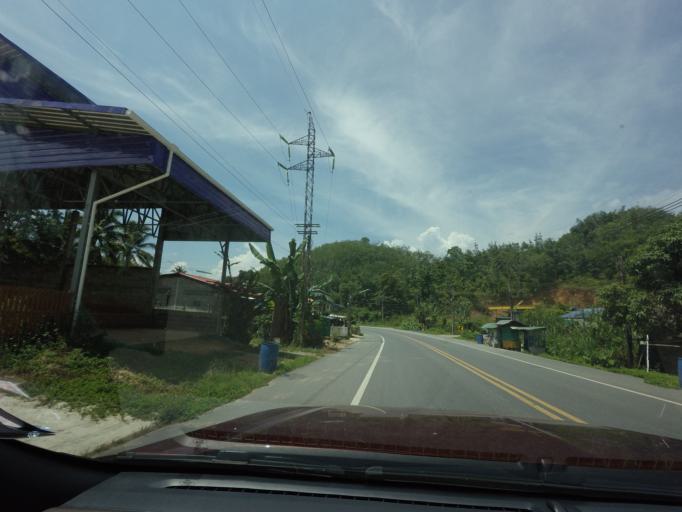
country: TH
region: Yala
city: Betong
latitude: 5.9167
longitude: 101.1710
